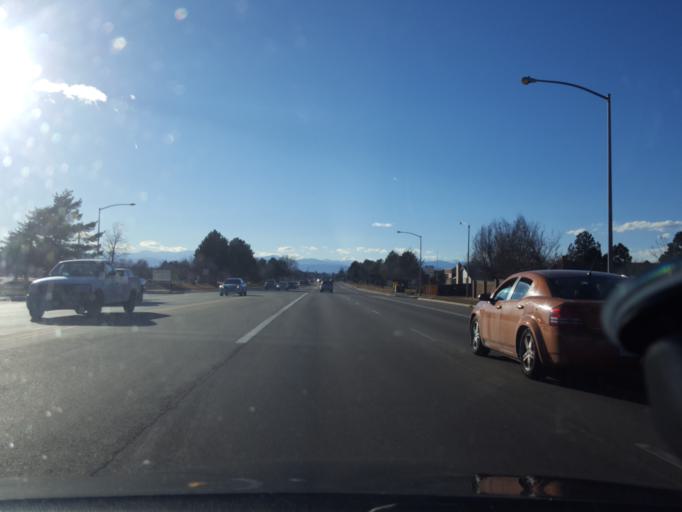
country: US
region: Colorado
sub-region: Adams County
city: Aurora
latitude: 39.7256
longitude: -104.8034
